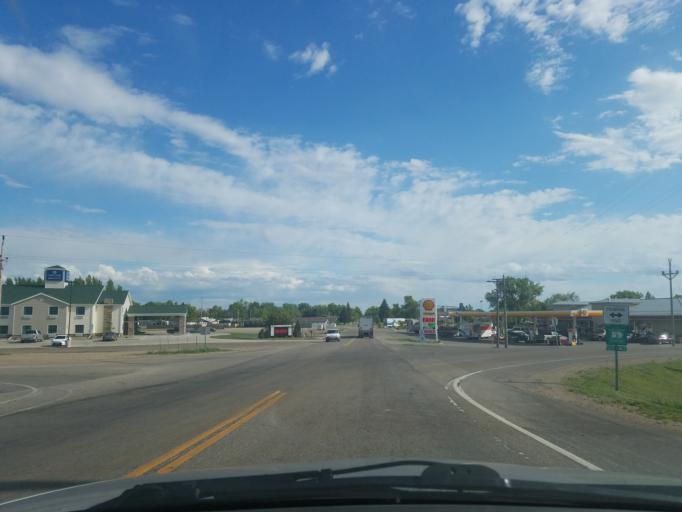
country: US
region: North Dakota
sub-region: Kidder County
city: Steele
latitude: 46.8627
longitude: -99.9157
